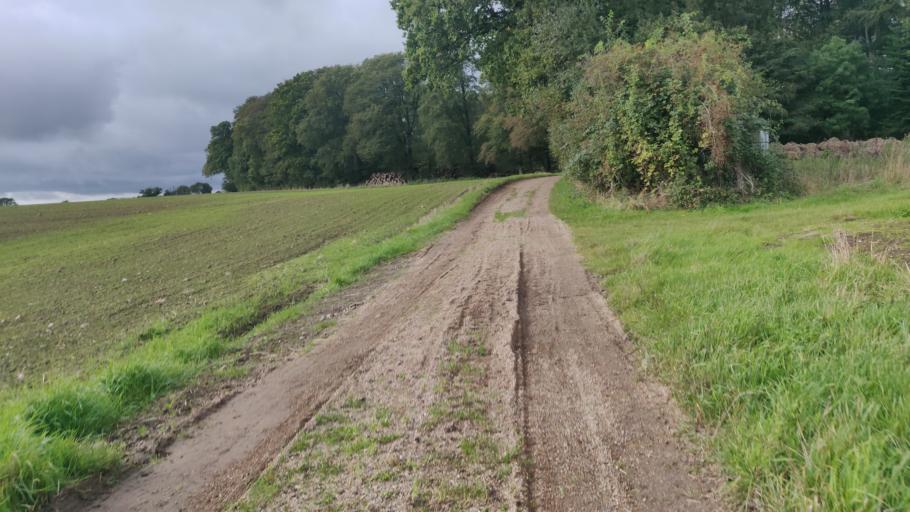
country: DK
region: South Denmark
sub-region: Kolding Kommune
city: Lunderskov
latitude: 55.5390
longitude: 9.3610
